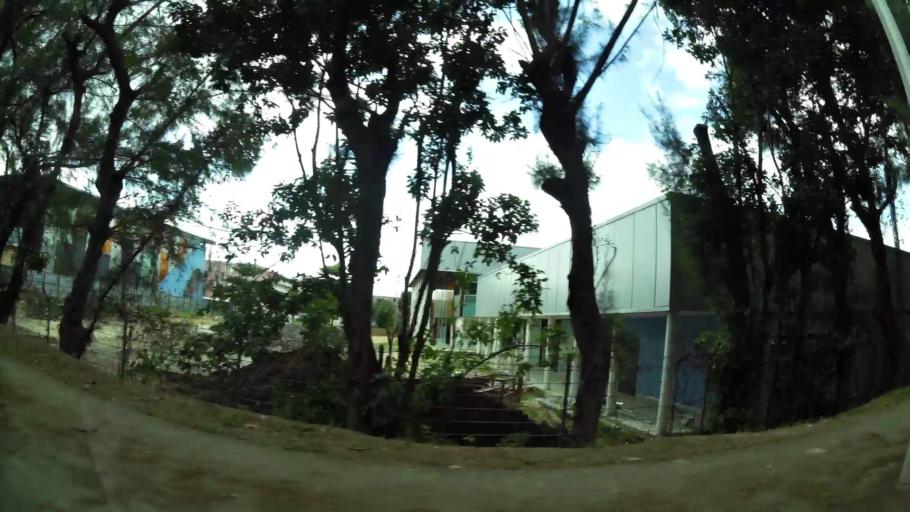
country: GP
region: Guadeloupe
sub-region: Guadeloupe
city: Pointe-a-Pitre
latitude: 16.2476
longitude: -61.5359
